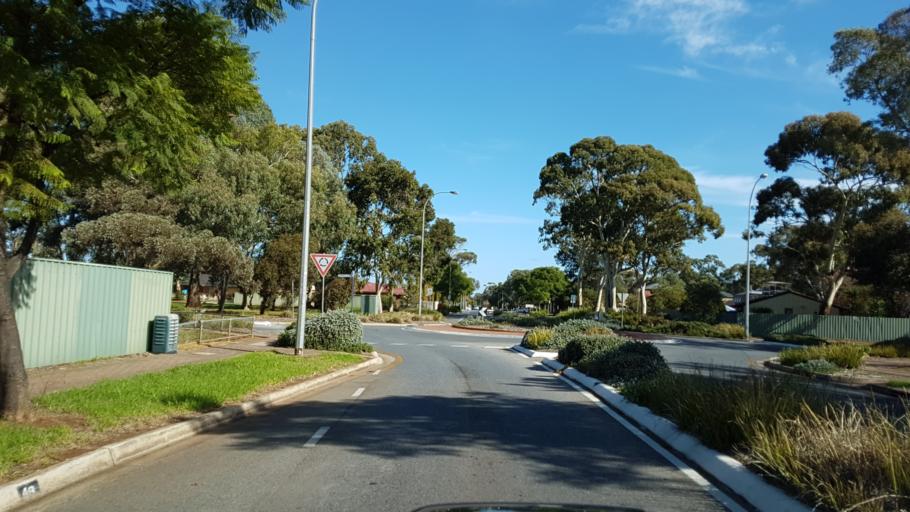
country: AU
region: South Australia
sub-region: Salisbury
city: Salisbury
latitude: -34.7503
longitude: 138.6362
